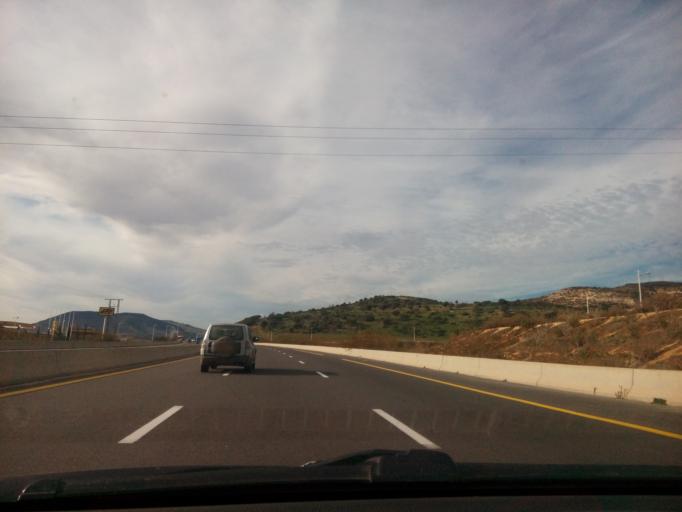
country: DZ
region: Sidi Bel Abbes
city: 'Ain el Berd
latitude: 35.4327
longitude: -0.4562
